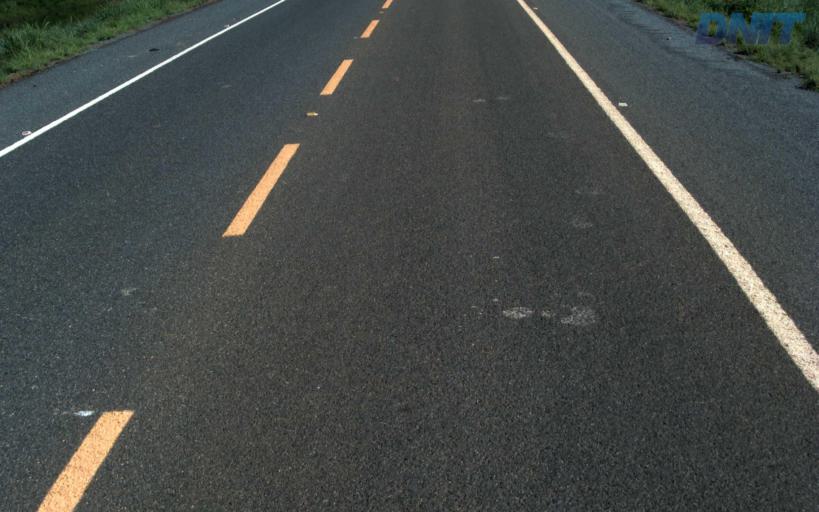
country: BR
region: Goias
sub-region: Sao Miguel Do Araguaia
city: Sao Miguel do Araguaia
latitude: -13.4635
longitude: -50.1169
